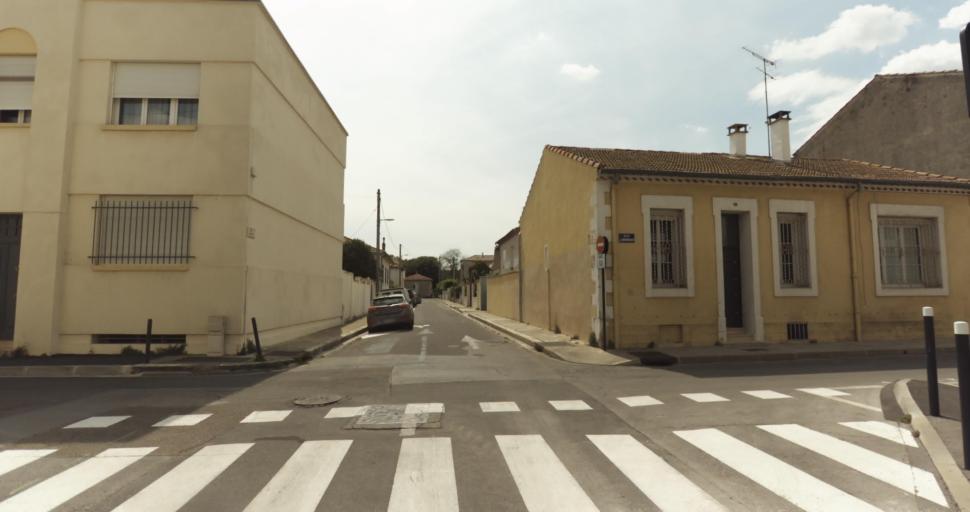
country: FR
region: Languedoc-Roussillon
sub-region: Departement du Gard
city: Nimes
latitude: 43.8298
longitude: 4.3666
